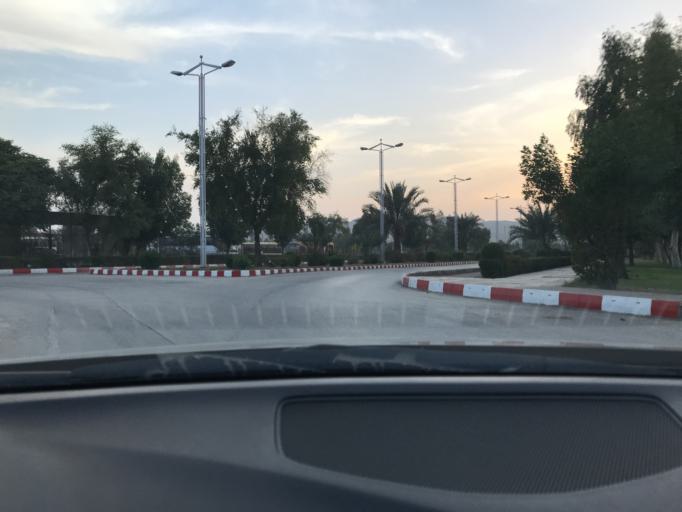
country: IR
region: Khuzestan
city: Ahvaz
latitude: 31.3285
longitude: 48.7339
